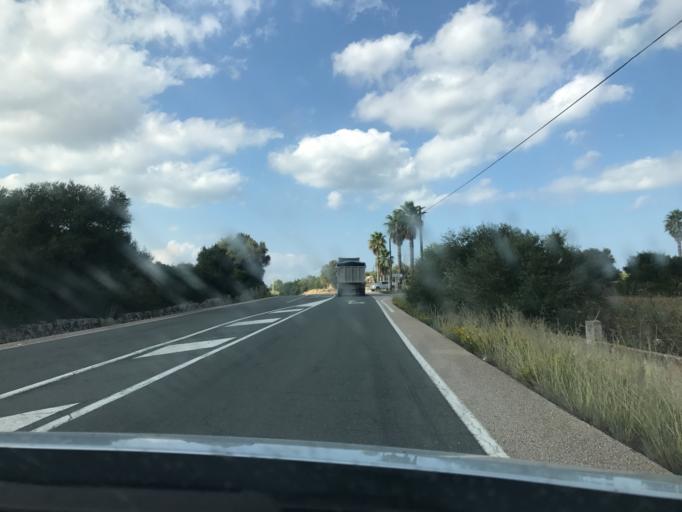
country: ES
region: Balearic Islands
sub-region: Illes Balears
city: Santa Margalida
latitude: 39.7227
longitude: 3.2105
